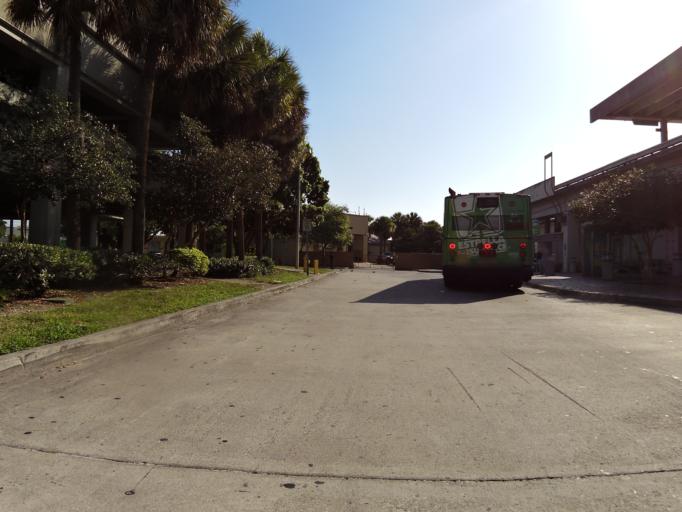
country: US
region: Florida
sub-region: Miami-Dade County
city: South Miami
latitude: 25.7053
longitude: -80.2891
